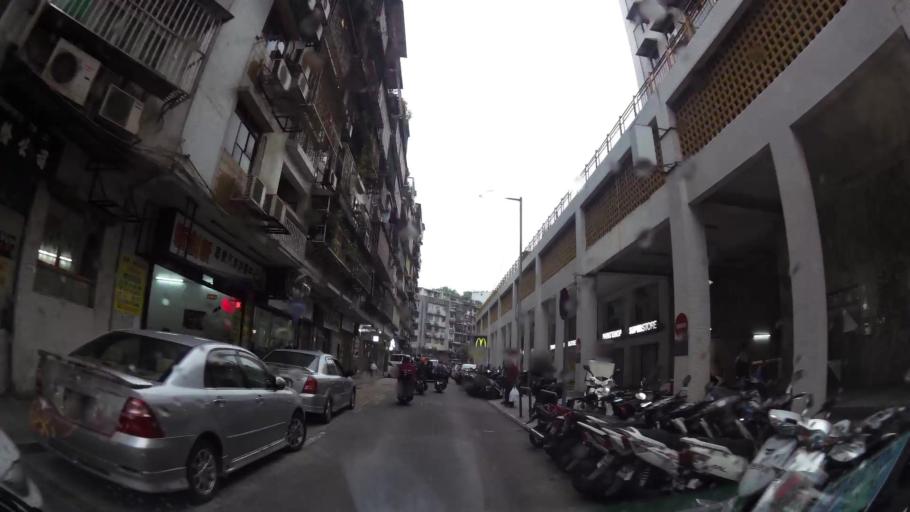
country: MO
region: Macau
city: Macau
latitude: 22.1988
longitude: 113.5443
